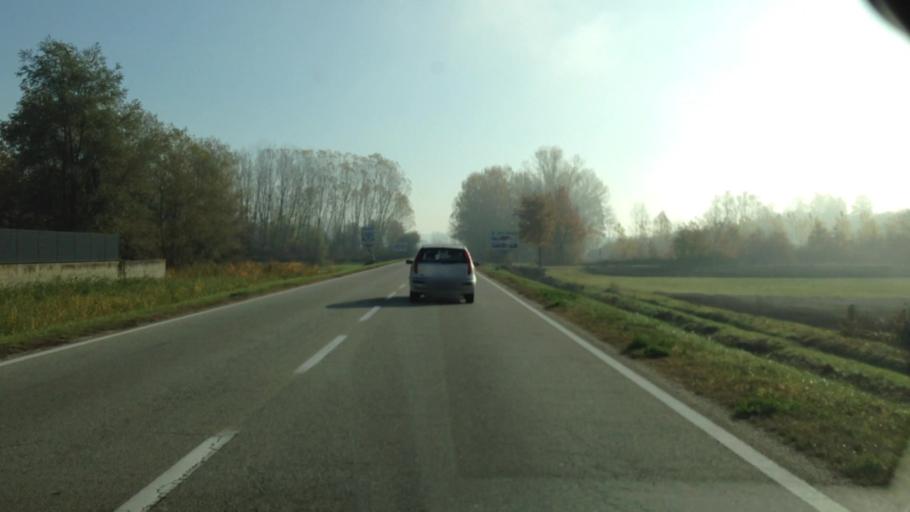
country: IT
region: Piedmont
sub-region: Provincia di Asti
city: Vigliano d'Asti
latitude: 44.8245
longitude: 8.2186
